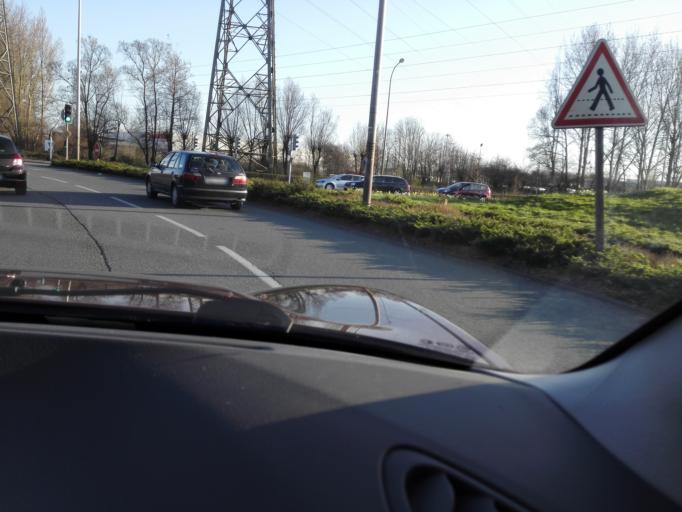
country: FR
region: Nord-Pas-de-Calais
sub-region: Departement du Nord
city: Grande-Synthe
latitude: 51.0090
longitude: 2.2829
